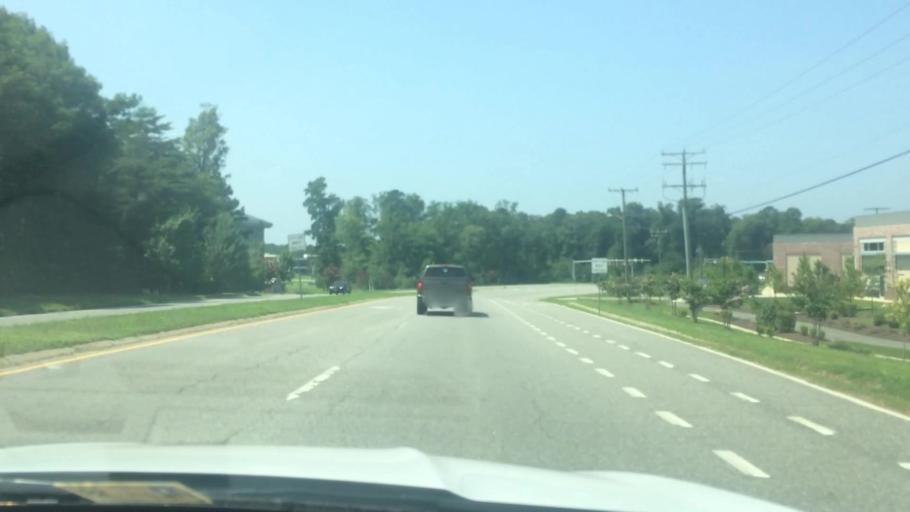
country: US
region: Virginia
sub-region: James City County
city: Williamsburg
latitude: 37.3382
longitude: -76.7549
